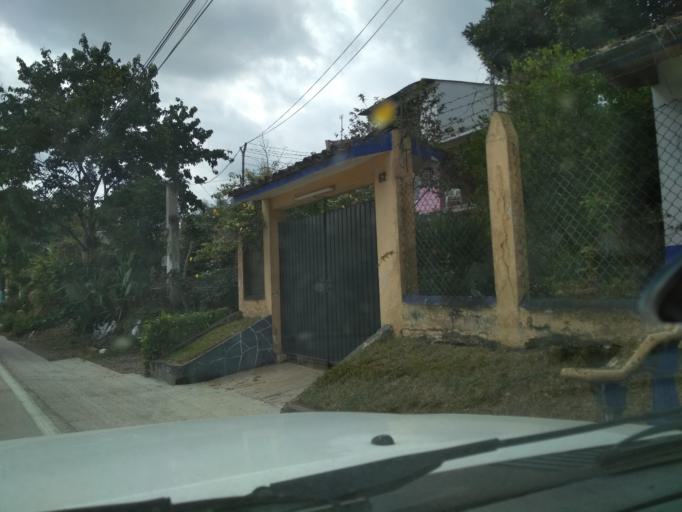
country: MX
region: Veracruz
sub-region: Coatepec
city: Bella Esperanza
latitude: 19.4564
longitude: -96.8612
